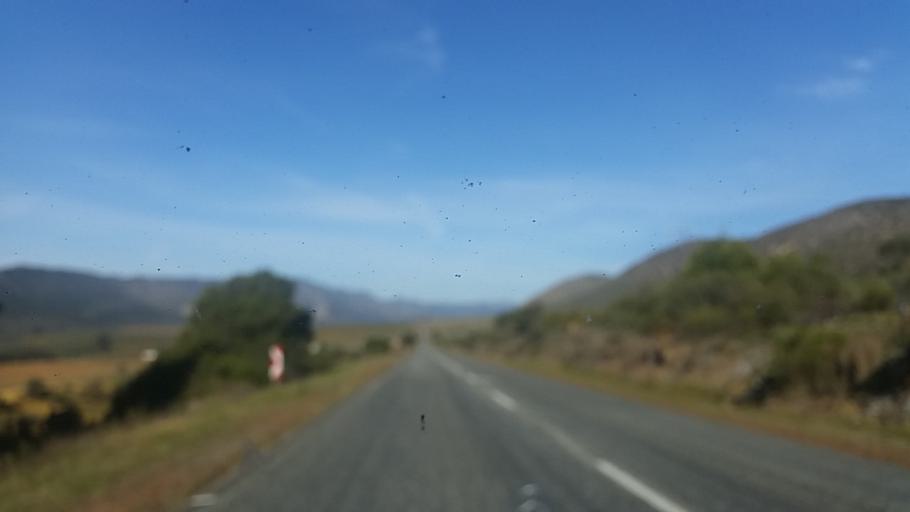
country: ZA
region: Western Cape
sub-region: Eden District Municipality
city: Knysna
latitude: -33.7728
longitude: 22.9229
